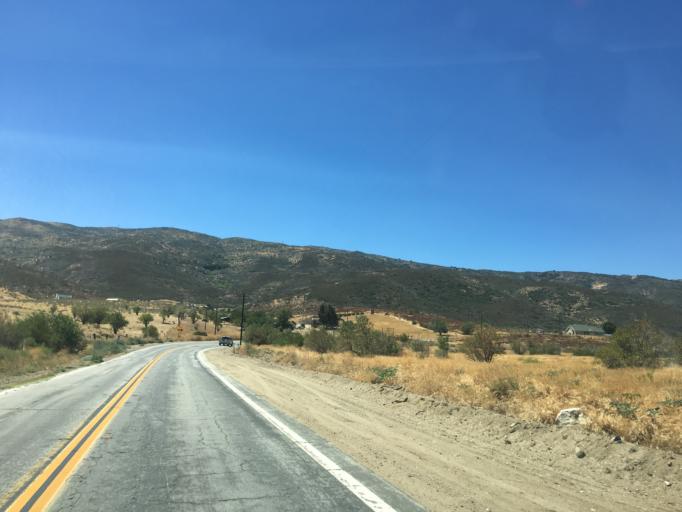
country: US
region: California
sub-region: Los Angeles County
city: Leona Valley
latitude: 34.5972
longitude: -118.2710
